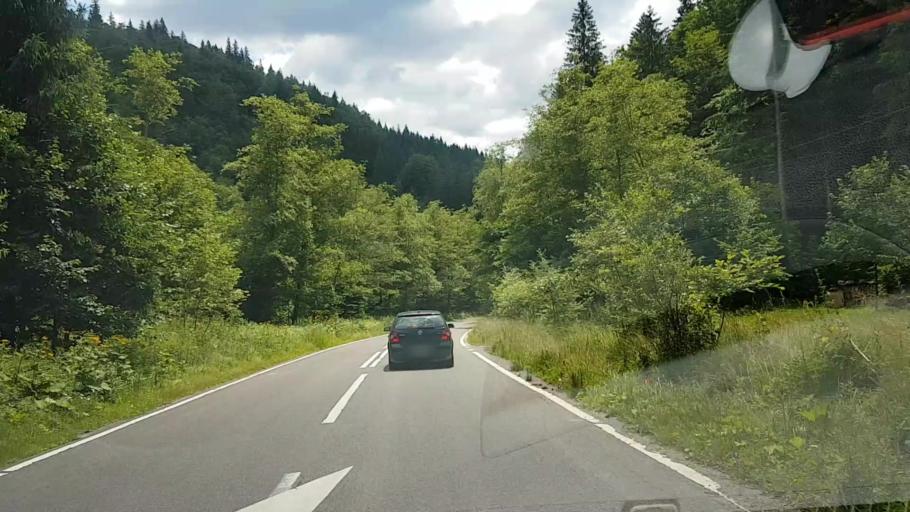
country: RO
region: Suceava
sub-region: Comuna Crucea
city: Crucea
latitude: 47.2992
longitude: 25.6317
